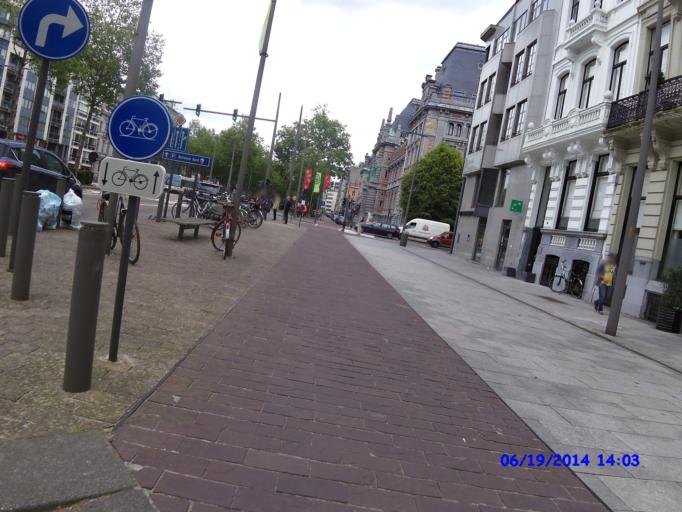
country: BE
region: Flanders
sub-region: Provincie Antwerpen
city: Antwerpen
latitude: 51.2085
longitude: 4.4021
